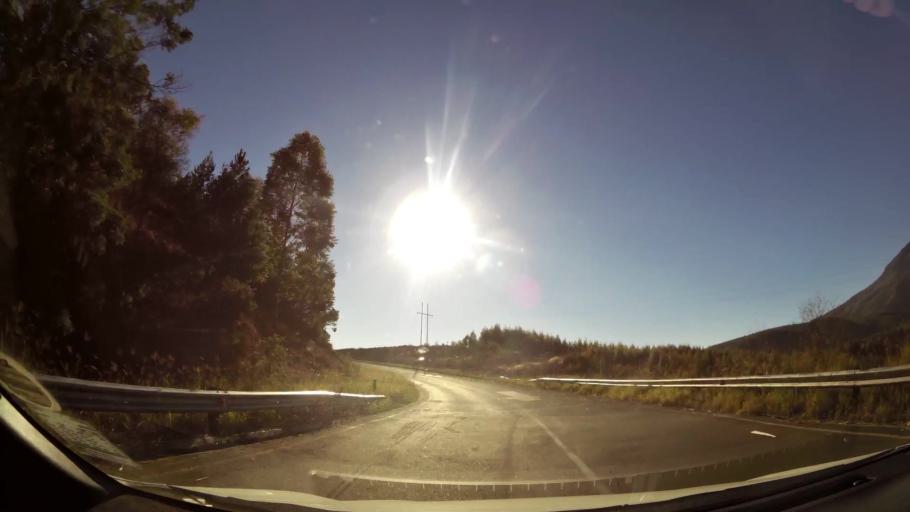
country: ZA
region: Limpopo
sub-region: Mopani District Municipality
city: Tzaneen
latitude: -23.9508
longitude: 30.0137
